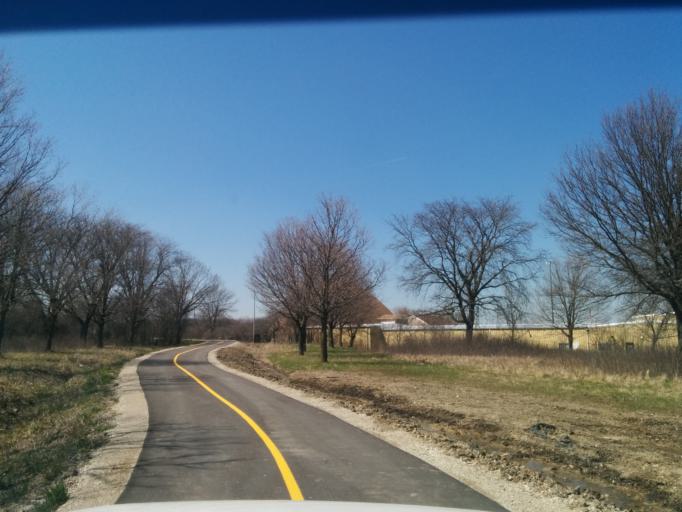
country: US
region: Illinois
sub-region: Cook County
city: Markham
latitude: 41.6009
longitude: -87.7177
